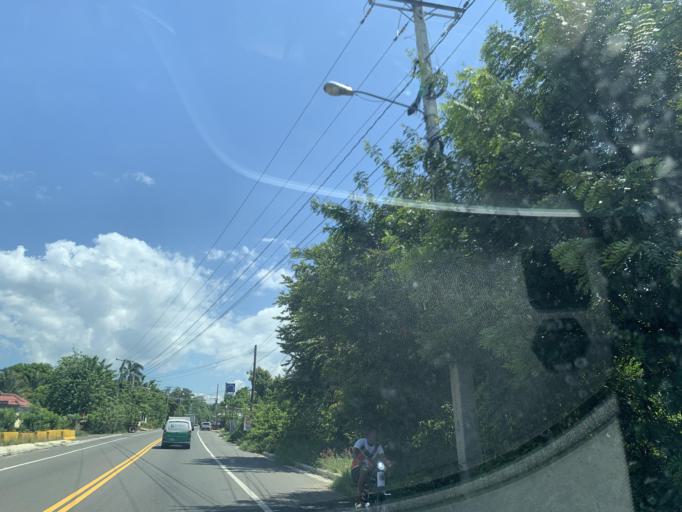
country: DO
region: Puerto Plata
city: Imbert
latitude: 19.7187
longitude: -70.8338
